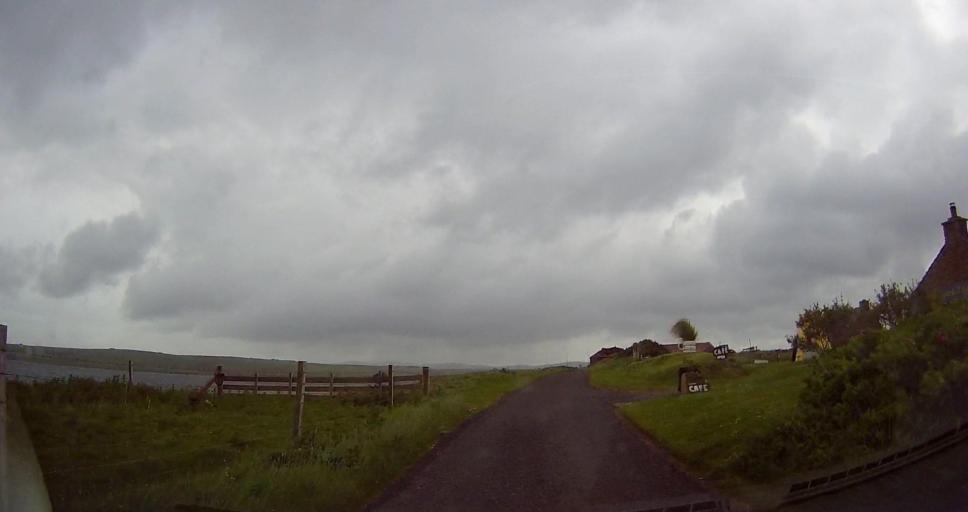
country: GB
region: Scotland
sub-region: Orkney Islands
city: Stromness
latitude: 58.9161
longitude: -3.3198
